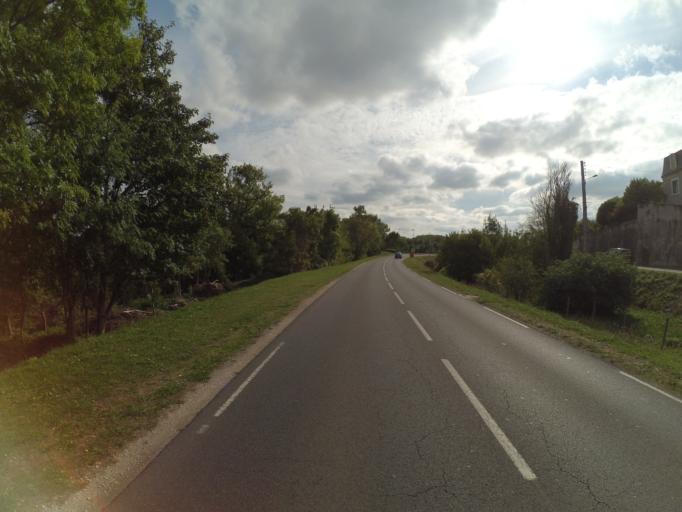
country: FR
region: Centre
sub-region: Departement d'Indre-et-Loire
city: Vernou-sur-Brenne
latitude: 47.4148
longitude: 0.8433
